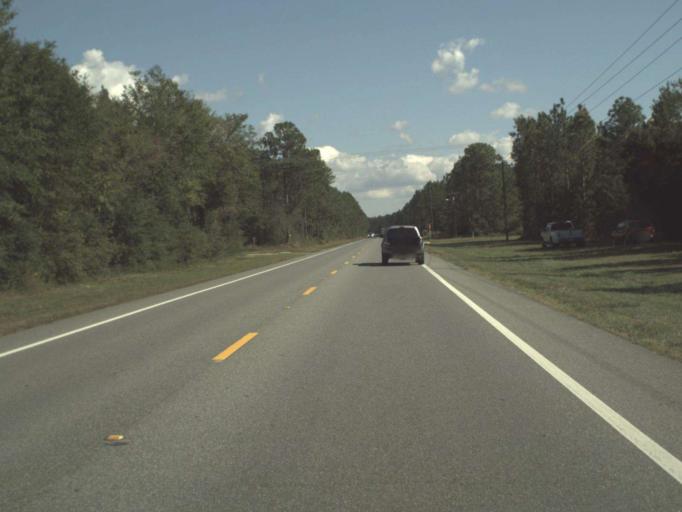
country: US
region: Florida
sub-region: Walton County
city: Freeport
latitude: 30.4856
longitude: -86.1094
